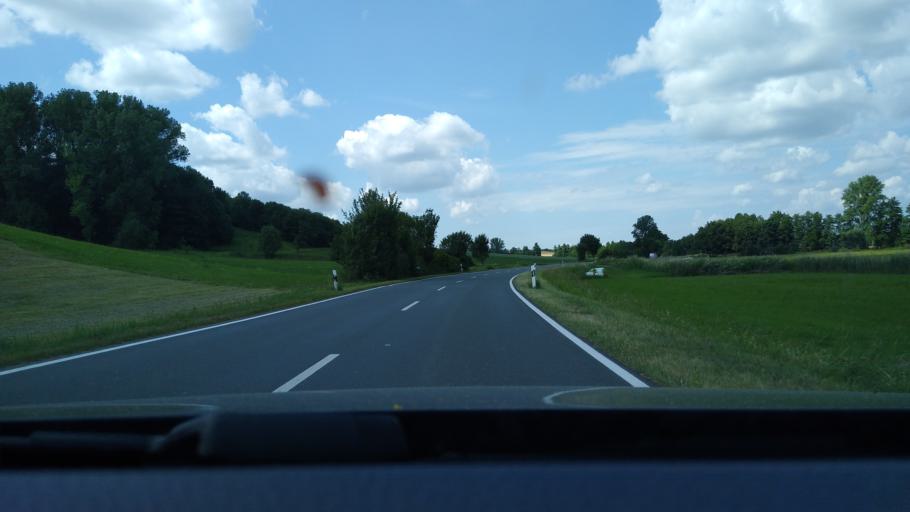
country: DE
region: Bavaria
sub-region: Regierungsbezirk Mittelfranken
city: Trautskirchen
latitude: 49.4606
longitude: 10.5537
